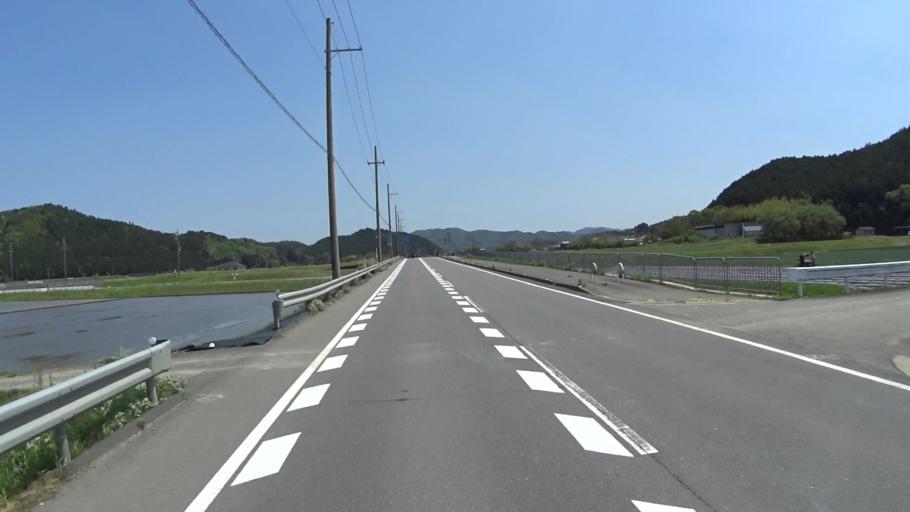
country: JP
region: Kyoto
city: Kameoka
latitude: 35.0464
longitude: 135.4791
